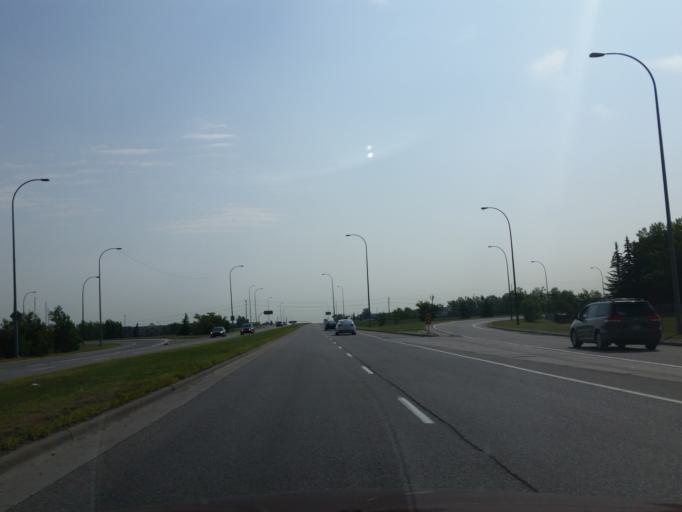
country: CA
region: Alberta
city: Calgary
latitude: 51.0668
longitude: -114.0084
